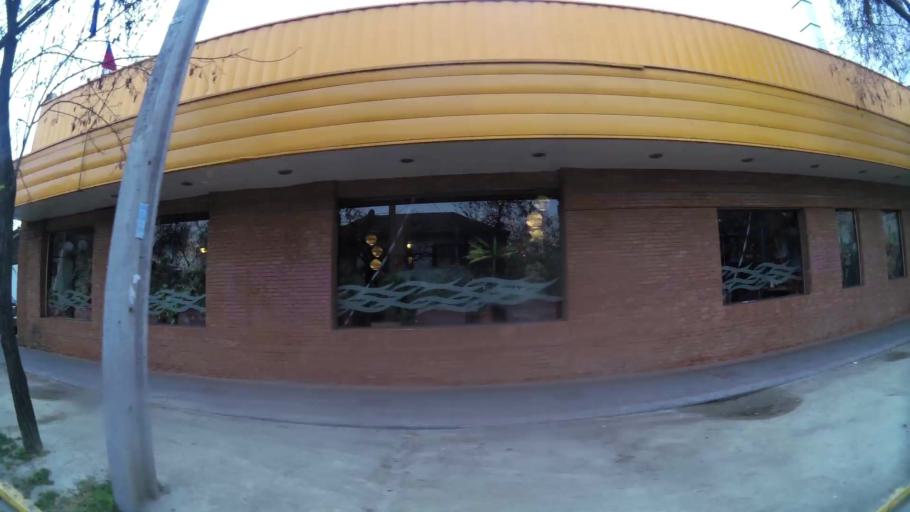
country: CL
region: Santiago Metropolitan
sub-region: Provincia de Santiago
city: Santiago
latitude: -33.4426
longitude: -70.6203
